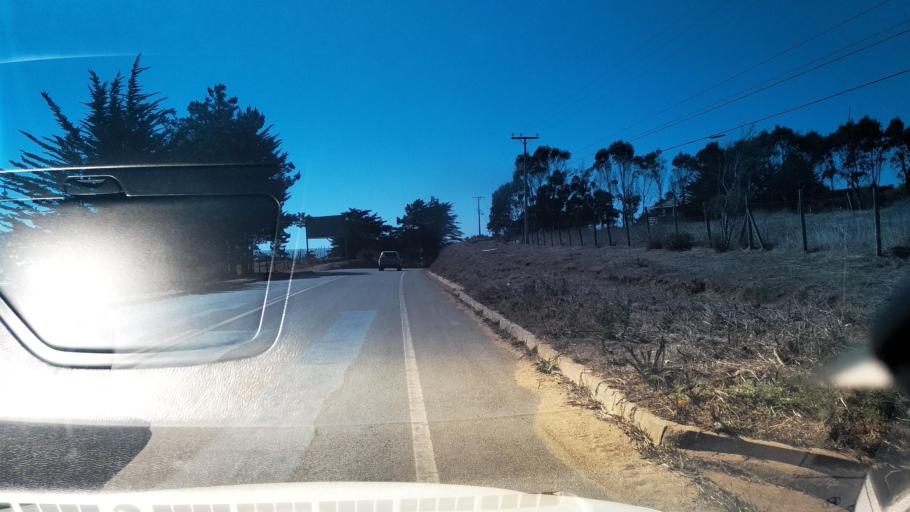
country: CL
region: O'Higgins
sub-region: Provincia de Colchagua
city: Santa Cruz
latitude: -34.4220
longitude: -72.0308
